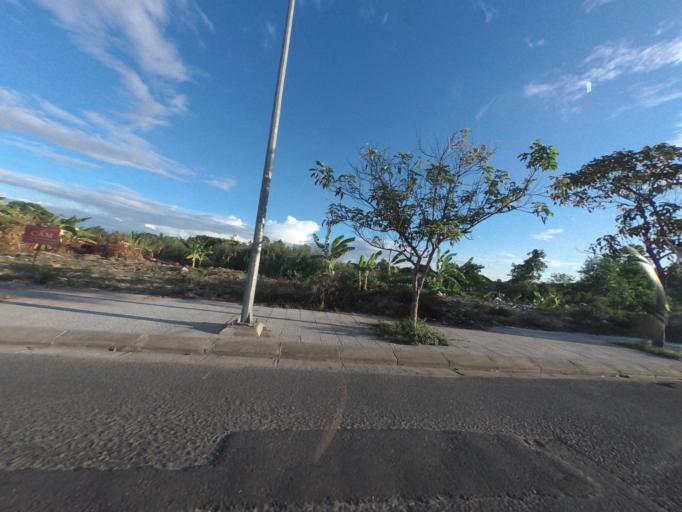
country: VN
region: Thua Thien-Hue
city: Hue
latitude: 16.4887
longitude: 107.5855
